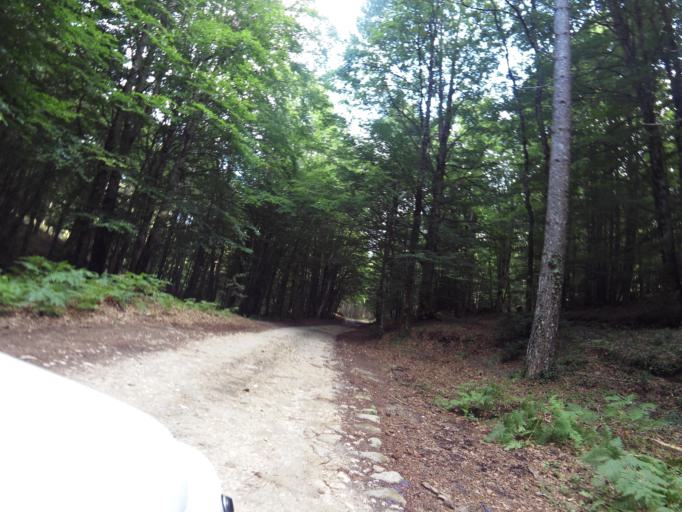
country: IT
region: Calabria
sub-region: Provincia di Vibo-Valentia
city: Nardodipace
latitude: 38.5124
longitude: 16.3791
